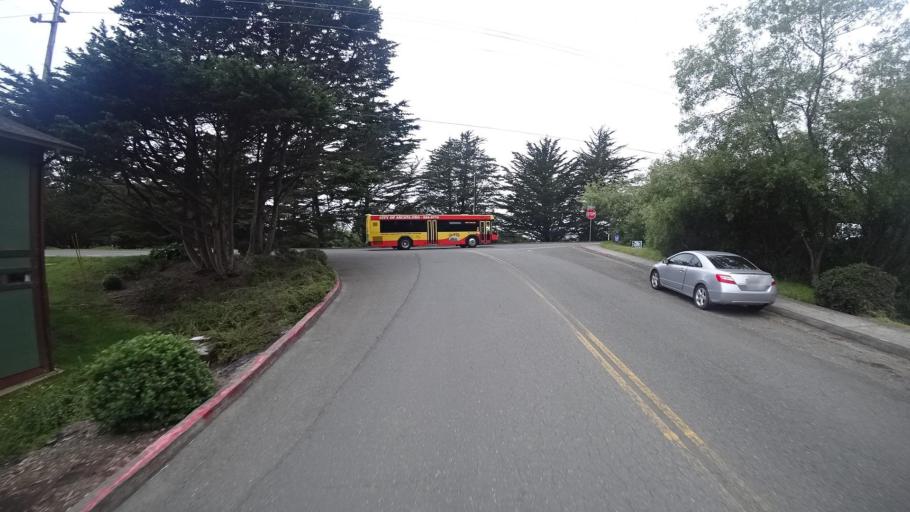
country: US
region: California
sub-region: Humboldt County
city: Arcata
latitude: 40.8883
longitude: -124.0788
